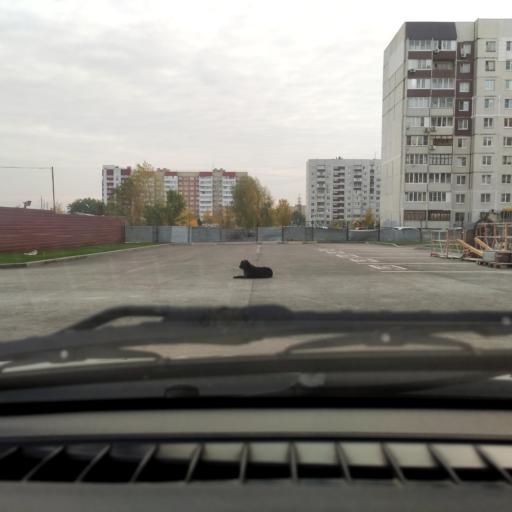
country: RU
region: Samara
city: Tol'yatti
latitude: 53.5422
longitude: 49.3973
